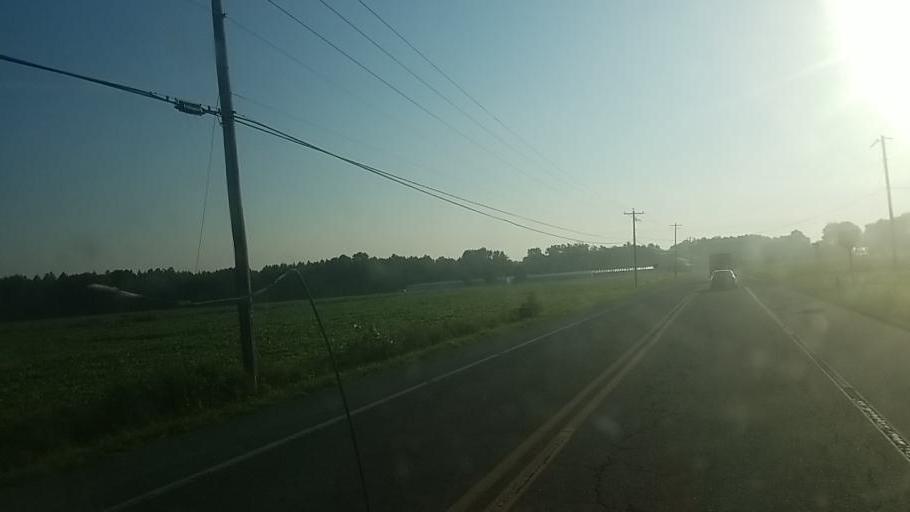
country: US
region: Delaware
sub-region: Sussex County
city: Selbyville
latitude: 38.4609
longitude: -75.1935
